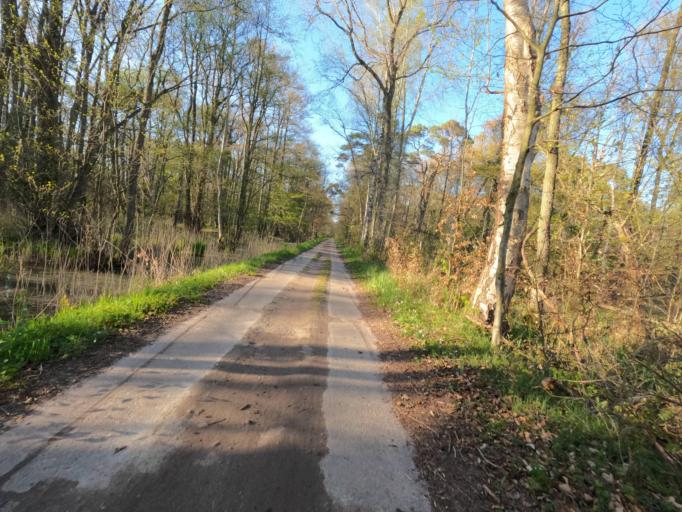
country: DE
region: Mecklenburg-Vorpommern
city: Ostseebad Prerow
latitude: 54.4332
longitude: 12.5398
